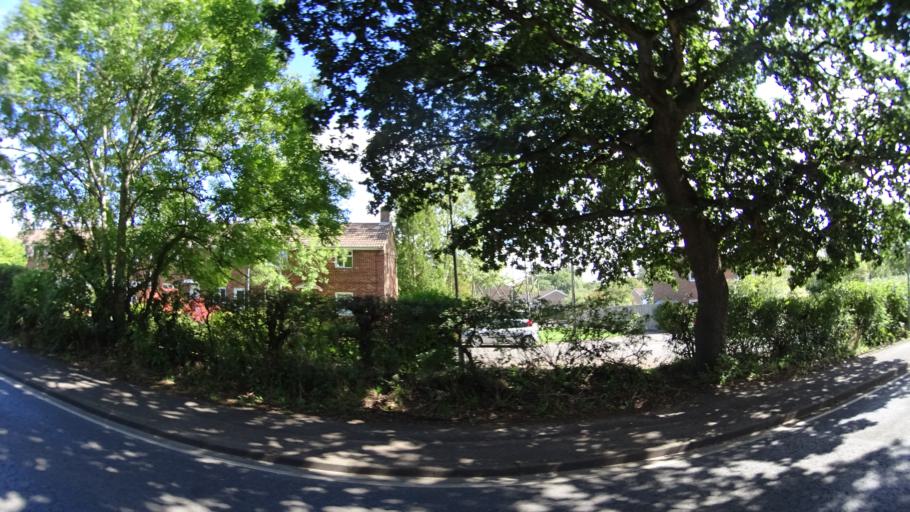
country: GB
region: England
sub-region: Hampshire
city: Romsey
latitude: 51.0026
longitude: -1.4727
